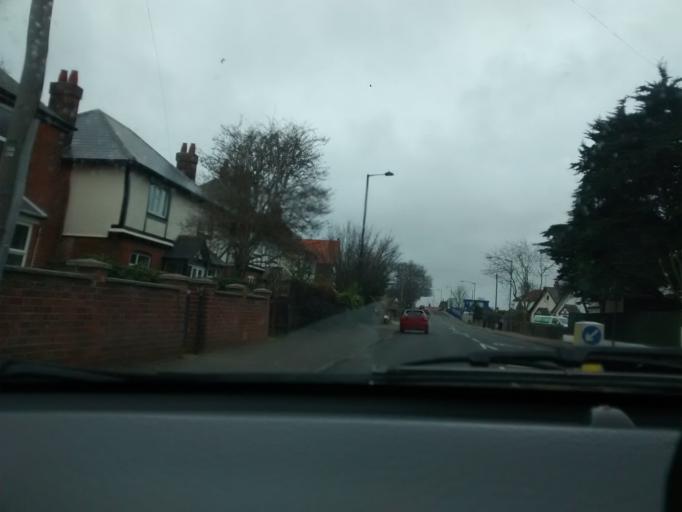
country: GB
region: England
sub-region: Suffolk
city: Felixstowe
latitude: 51.9651
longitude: 1.3453
